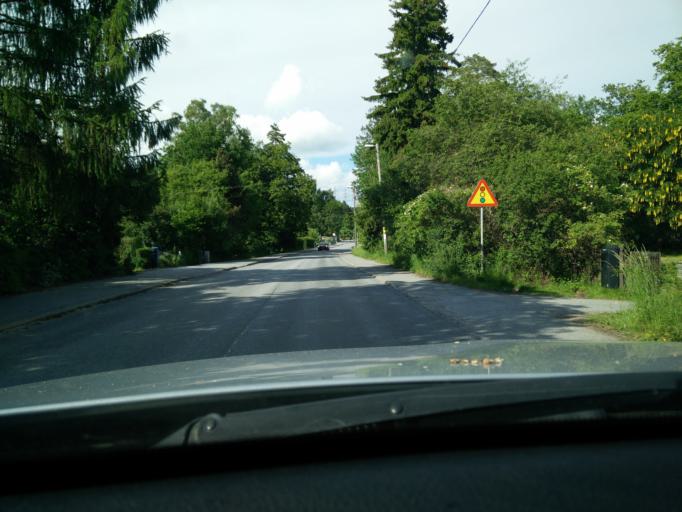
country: SE
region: Stockholm
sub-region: Sollentuna Kommun
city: Sollentuna
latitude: 59.4512
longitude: 17.9537
